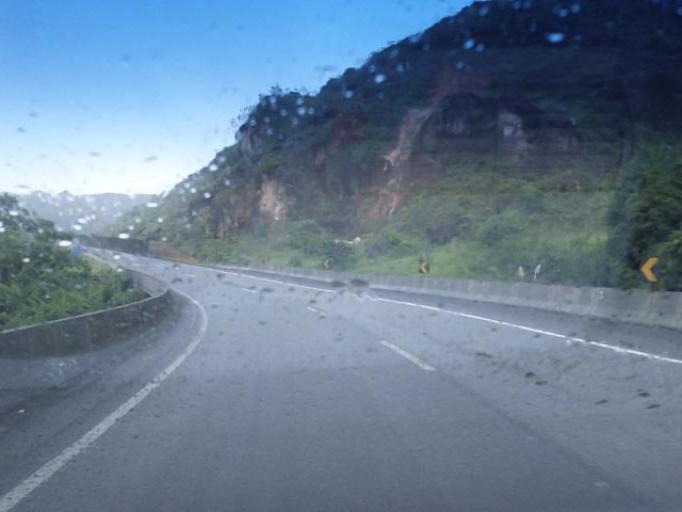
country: BR
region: Sao Paulo
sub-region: Cajati
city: Cajati
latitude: -24.9669
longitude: -48.4661
